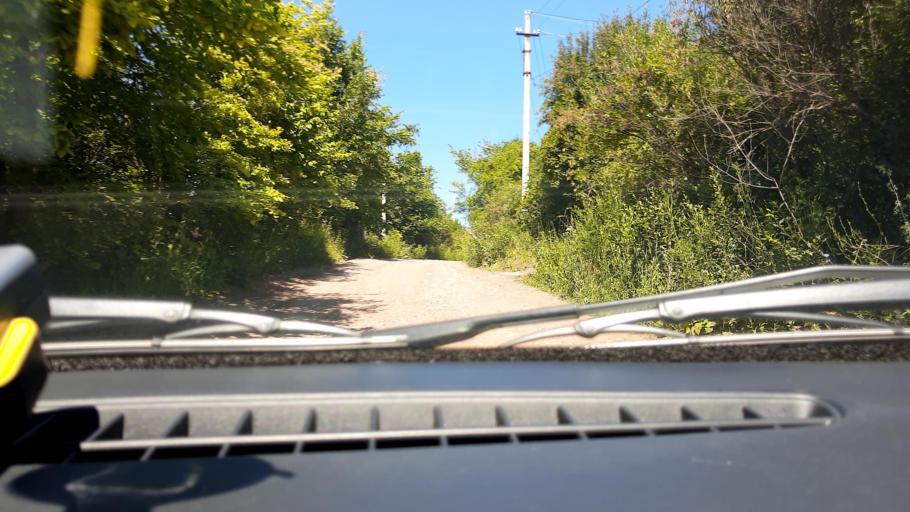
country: RU
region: Bashkortostan
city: Karmaskaly
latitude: 54.3612
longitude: 55.8954
